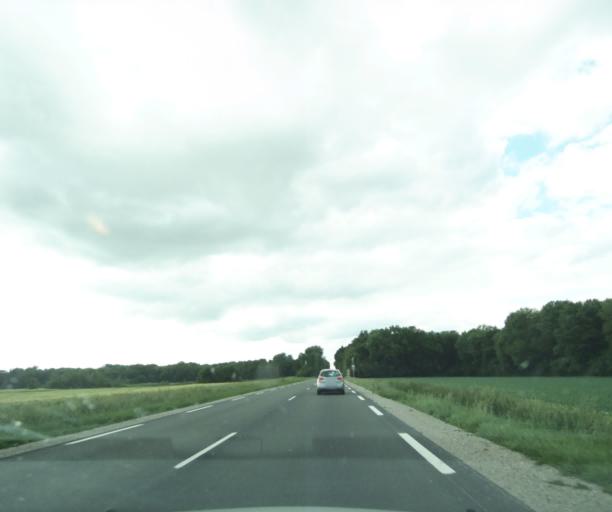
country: FR
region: Centre
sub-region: Departement d'Eure-et-Loir
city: Sours
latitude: 48.4003
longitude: 1.5551
